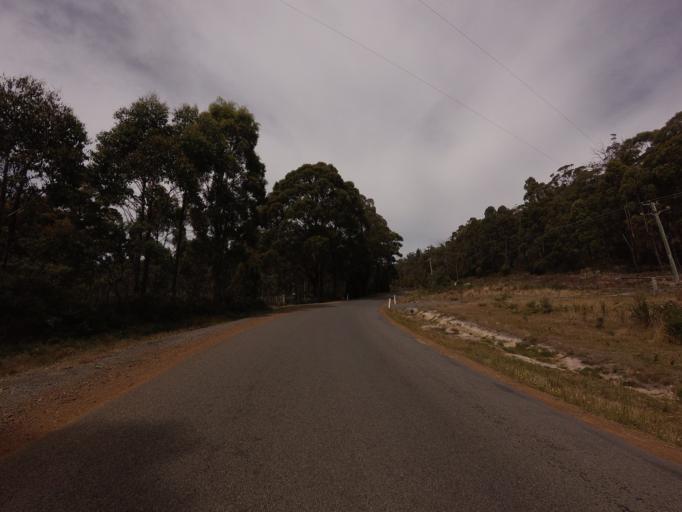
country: AU
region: Tasmania
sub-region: Sorell
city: Sorell
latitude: -42.5829
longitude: 147.5583
